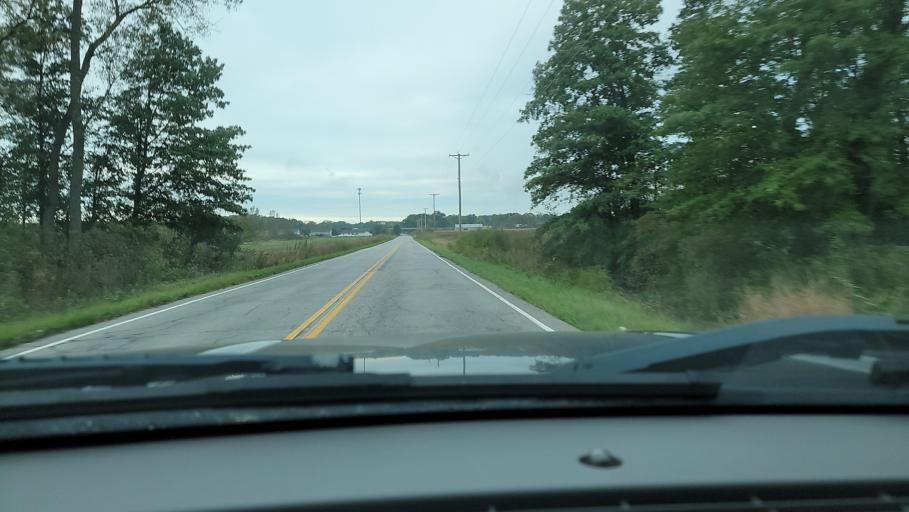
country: US
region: Indiana
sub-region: Porter County
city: Portage
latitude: 41.5681
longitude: -87.1535
